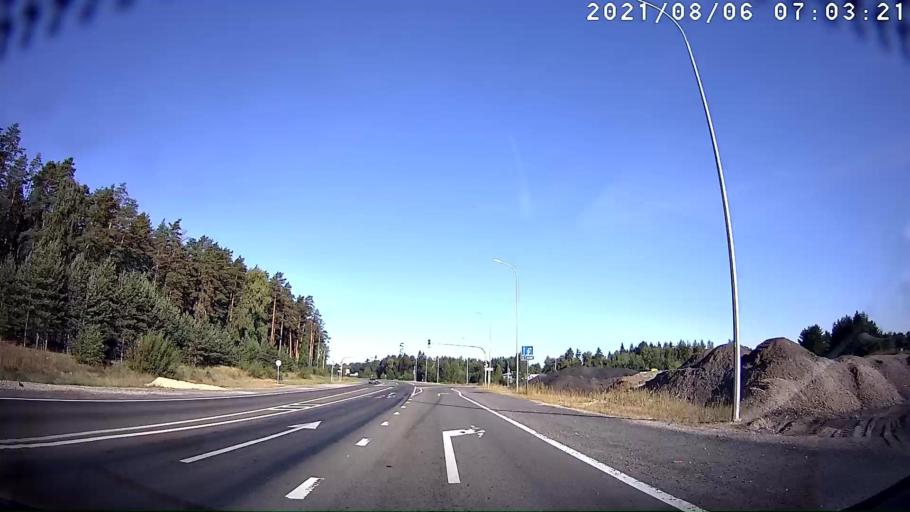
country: RU
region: Mariy-El
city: Yoshkar-Ola
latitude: 56.5408
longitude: 47.9844
